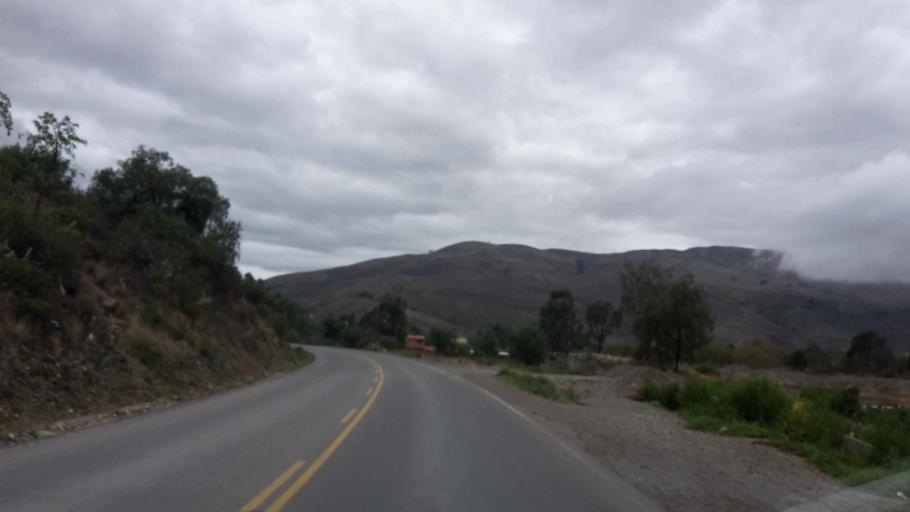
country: BO
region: Cochabamba
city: Punata
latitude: -17.5150
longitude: -65.8195
